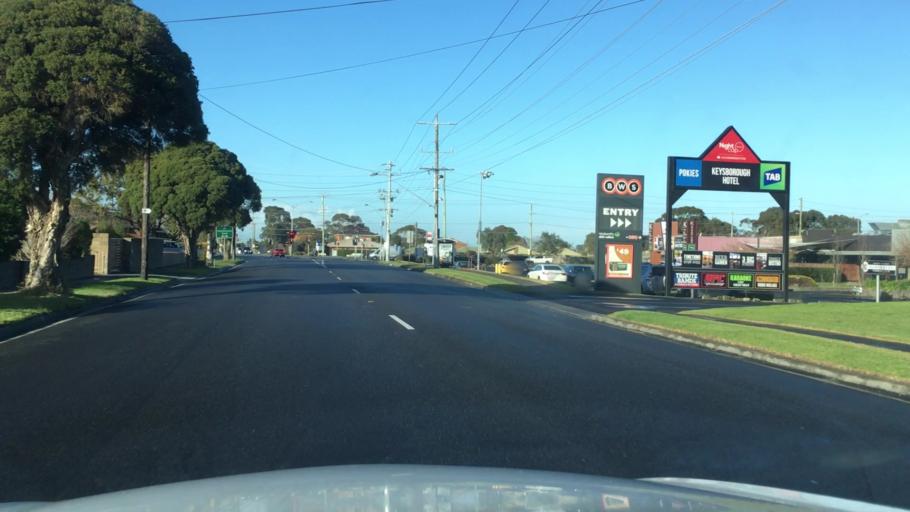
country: AU
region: Victoria
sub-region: Greater Dandenong
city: Keysborough
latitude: -37.9915
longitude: 145.1632
